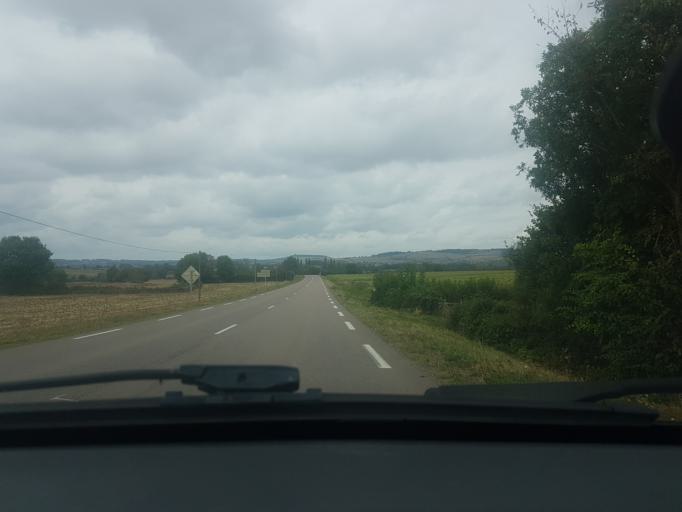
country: FR
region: Bourgogne
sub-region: Departement de la Cote-d'Or
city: Arnay-le-Duc
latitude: 47.1797
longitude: 4.4151
